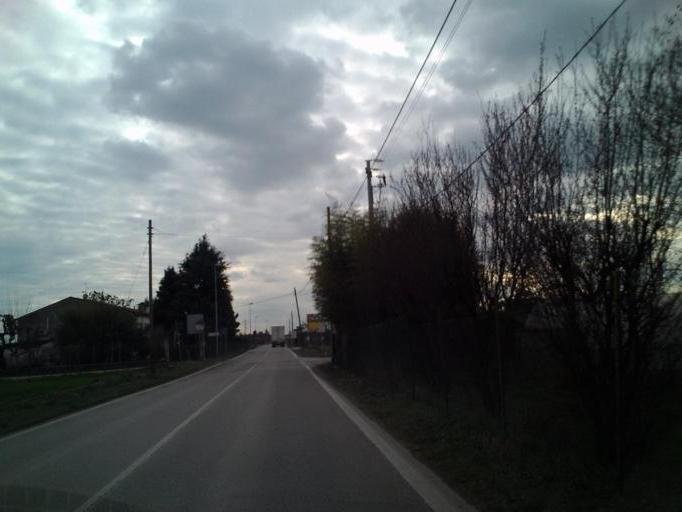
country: IT
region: Veneto
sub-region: Provincia di Verona
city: Alpo
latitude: 45.3855
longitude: 10.9301
